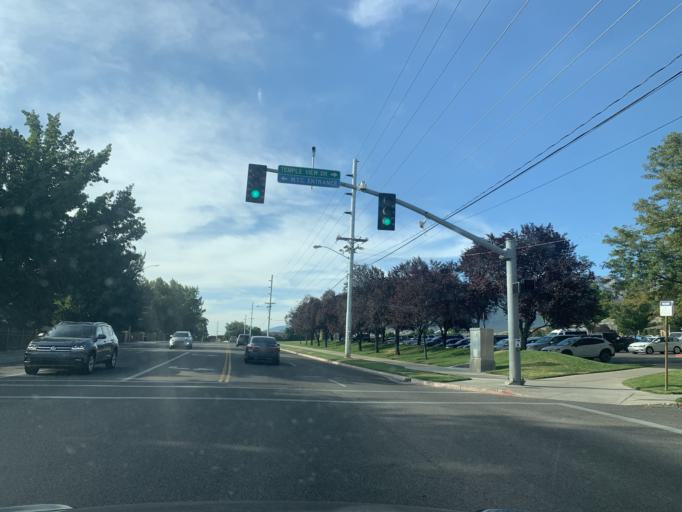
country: US
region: Utah
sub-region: Utah County
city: Provo
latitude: 40.2600
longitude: -111.6435
